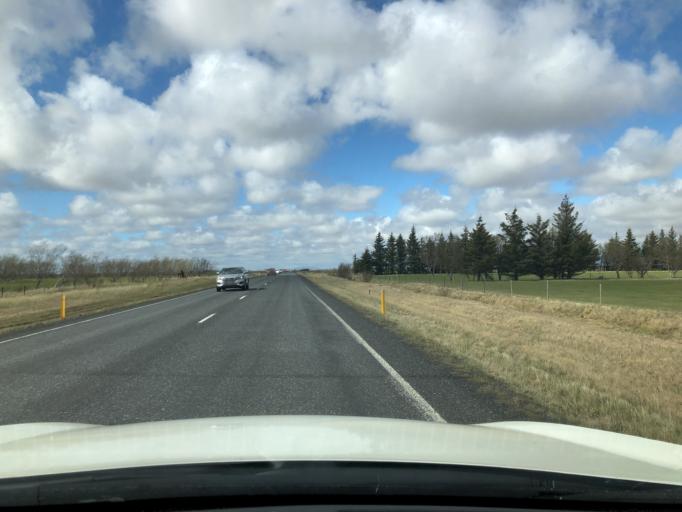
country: IS
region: South
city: Vestmannaeyjar
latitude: 63.7615
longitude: -20.2527
